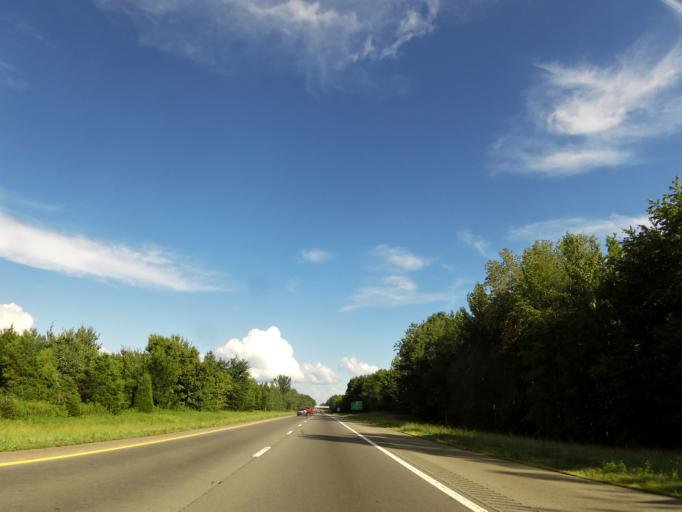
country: US
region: Tennessee
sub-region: Cheatham County
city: Pleasant View
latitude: 36.4148
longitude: -87.0466
